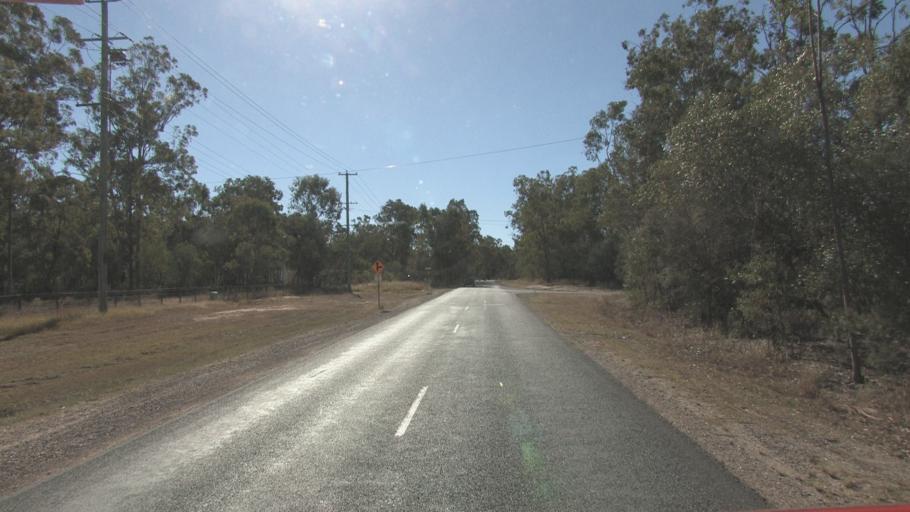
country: AU
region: Queensland
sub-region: Logan
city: North Maclean
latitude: -27.7601
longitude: 152.9960
